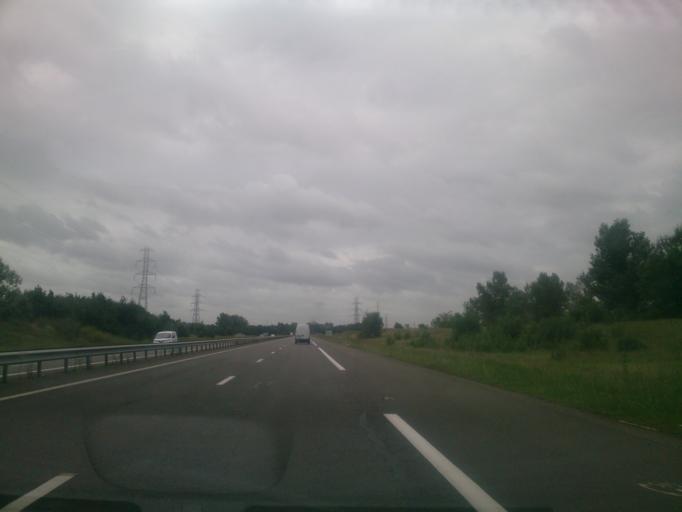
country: FR
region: Midi-Pyrenees
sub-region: Departement de la Haute-Garonne
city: Seysses
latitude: 43.4881
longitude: 1.3299
